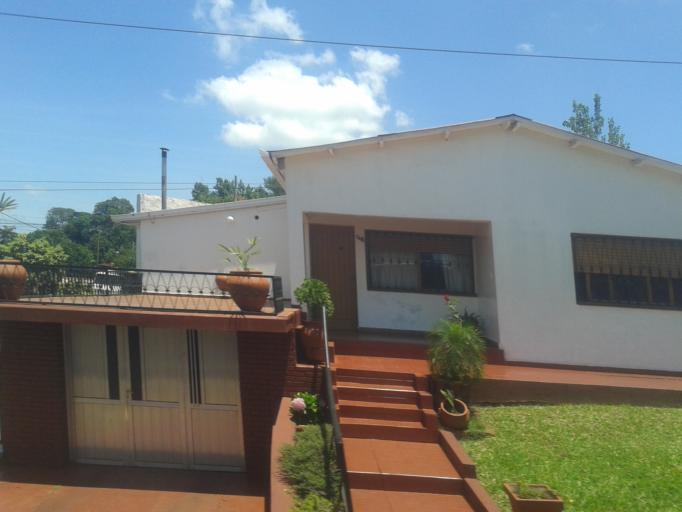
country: AR
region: Misiones
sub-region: Departamento de Leandro N. Alem
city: Leandro N. Alem
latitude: -27.6159
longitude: -55.3307
